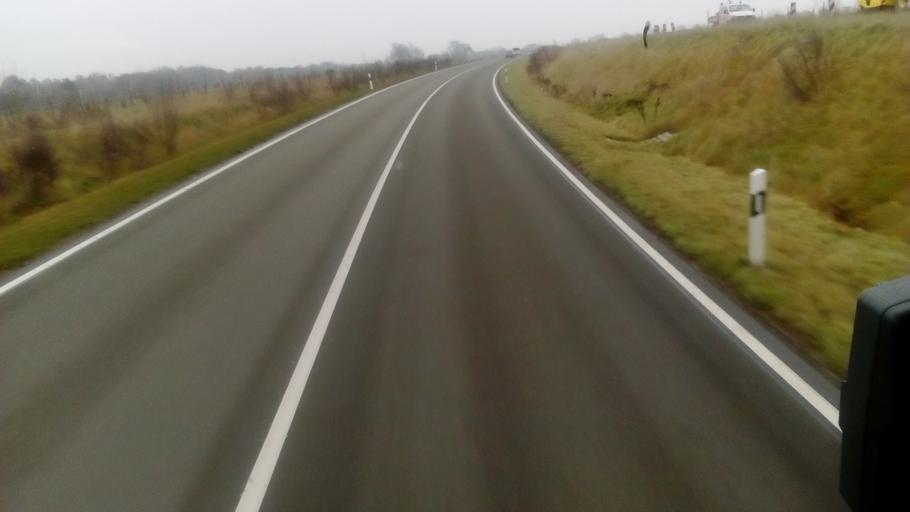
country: DE
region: Brandenburg
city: Gross Pankow
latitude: 53.1462
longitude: 12.0937
